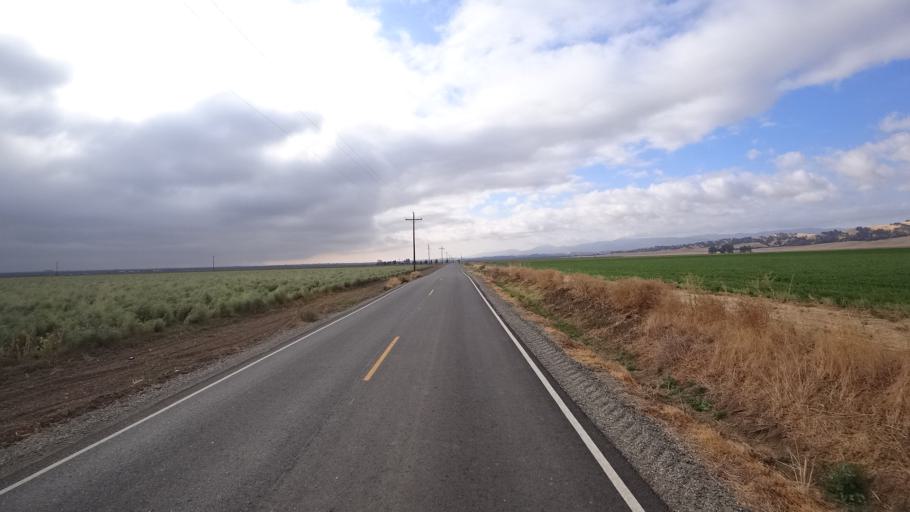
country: US
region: California
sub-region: Yolo County
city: Esparto
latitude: 38.7540
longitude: -122.0444
